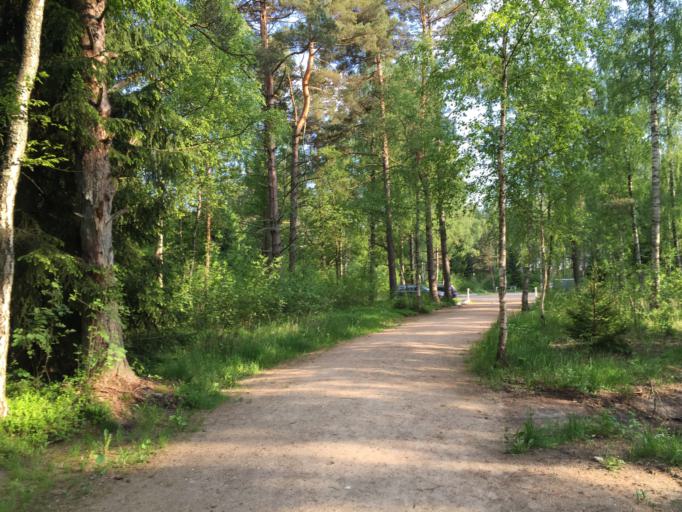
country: LT
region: Klaipedos apskritis
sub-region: Palanga
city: Sventoji
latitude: 56.0309
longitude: 21.1880
